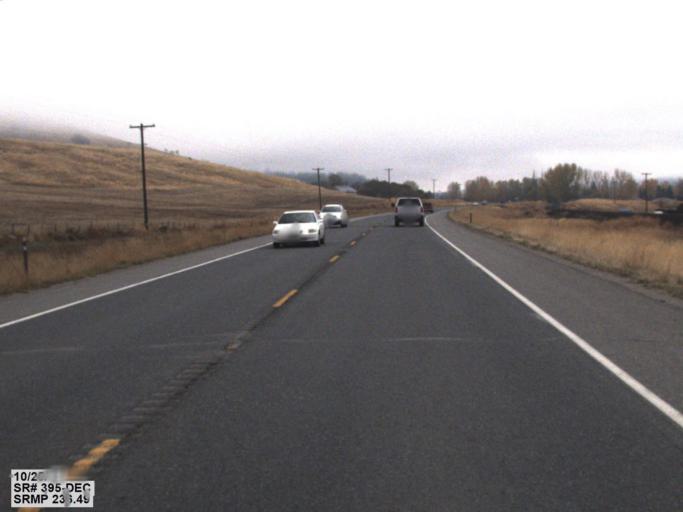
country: US
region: Washington
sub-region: Stevens County
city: Kettle Falls
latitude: 48.6037
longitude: -118.0224
